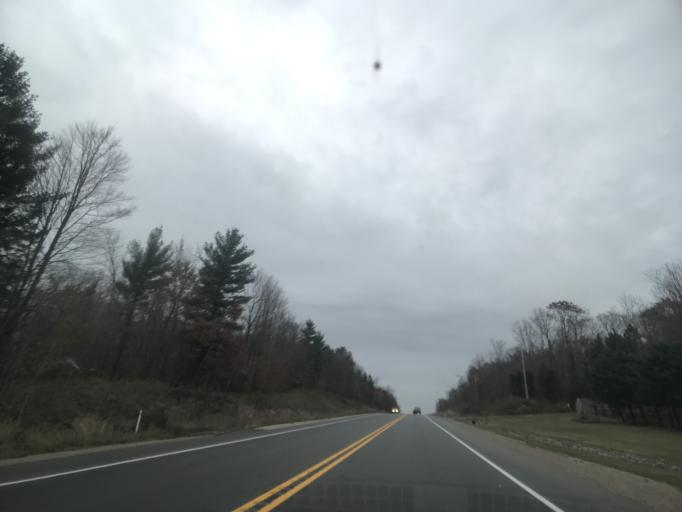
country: US
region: Wisconsin
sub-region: Menominee County
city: Legend Lake
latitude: 45.2442
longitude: -88.5152
